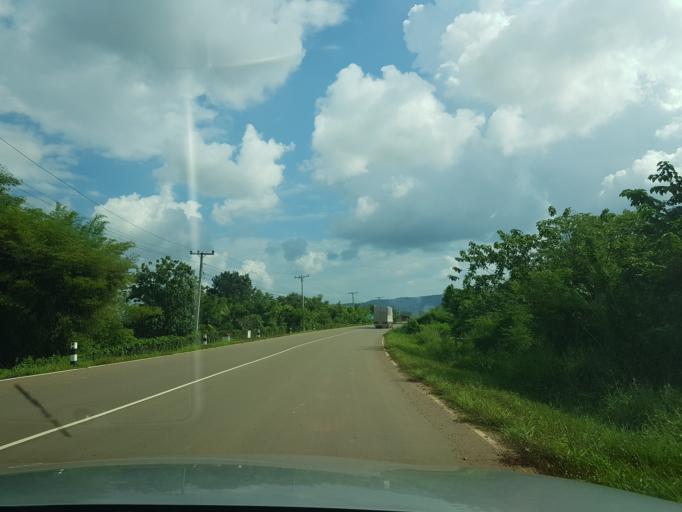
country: TH
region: Nong Khai
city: Sangkhom
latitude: 18.0849
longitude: 102.2927
